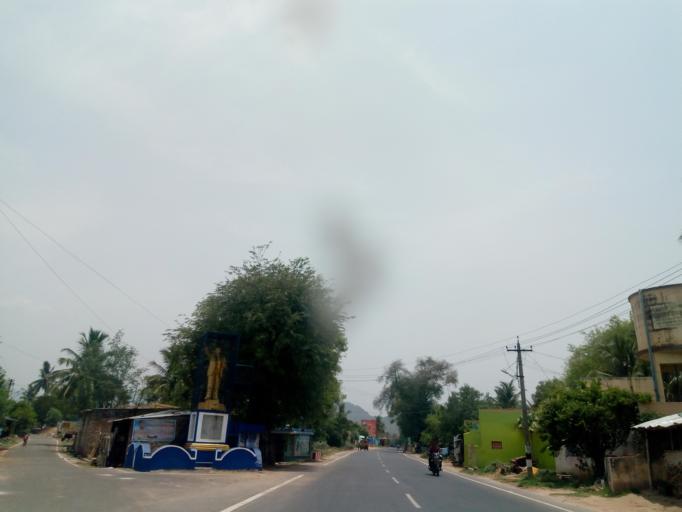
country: IN
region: Tamil Nadu
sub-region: Vellore
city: Vellore
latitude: 12.8744
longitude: 79.1017
